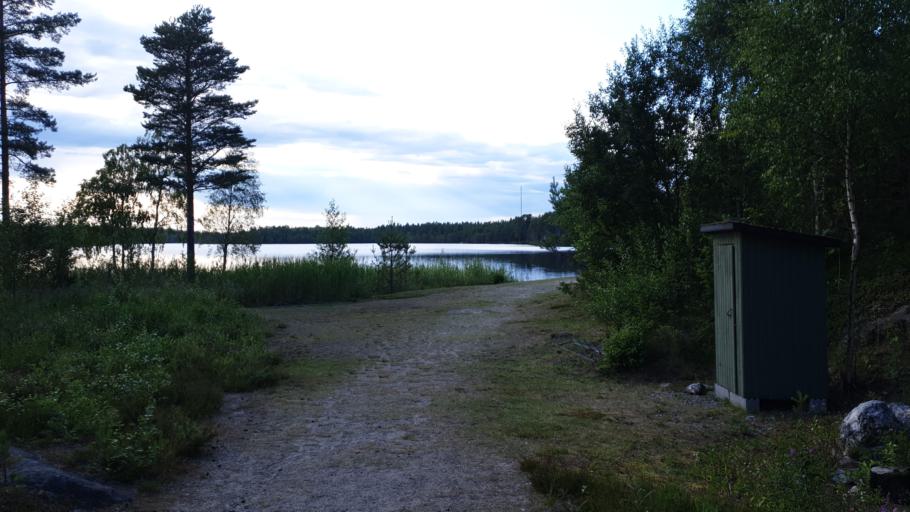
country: SE
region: Gaevleborg
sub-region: Soderhamns Kommun
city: Marielund
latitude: 61.4257
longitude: 17.1546
